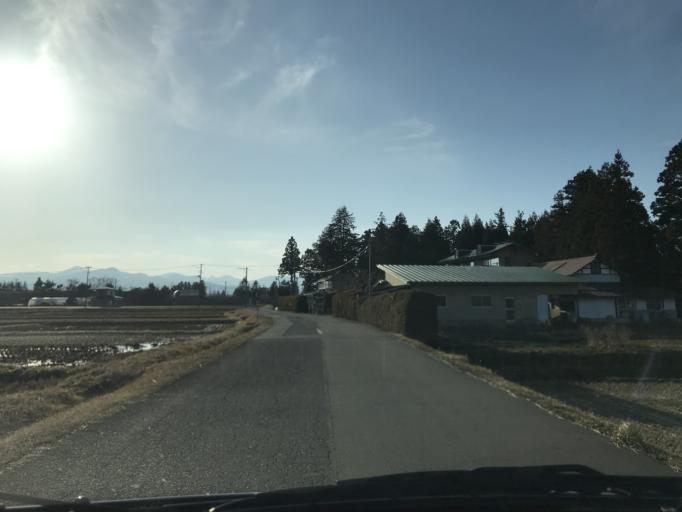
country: JP
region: Iwate
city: Kitakami
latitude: 39.2274
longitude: 141.0861
